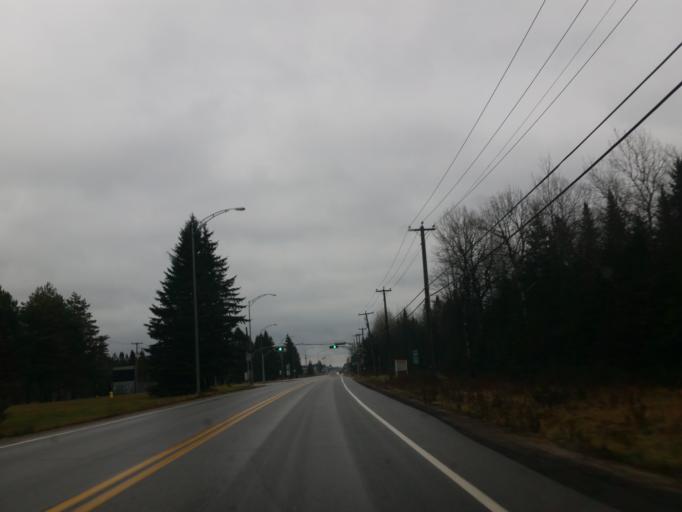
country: CA
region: Quebec
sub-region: Capitale-Nationale
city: Shannon
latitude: 46.8849
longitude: -71.4910
